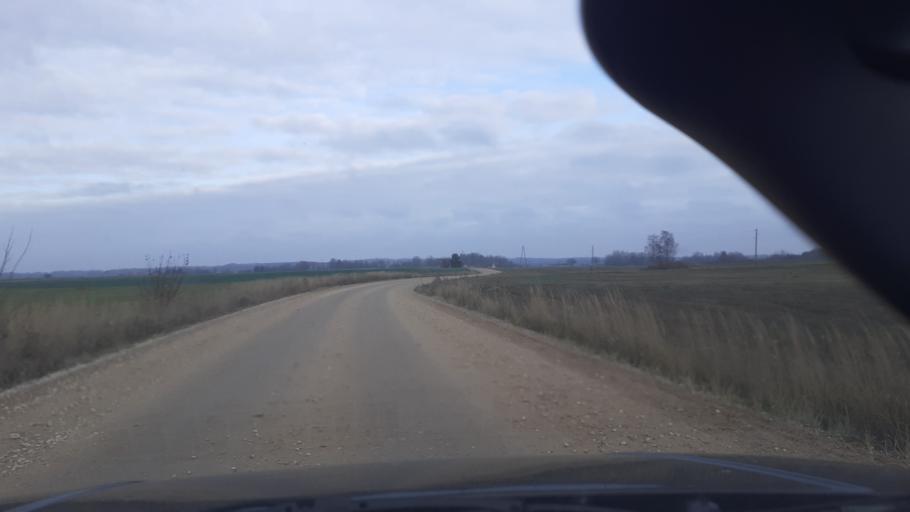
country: LV
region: Aizpute
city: Aizpute
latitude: 56.8507
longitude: 21.6658
